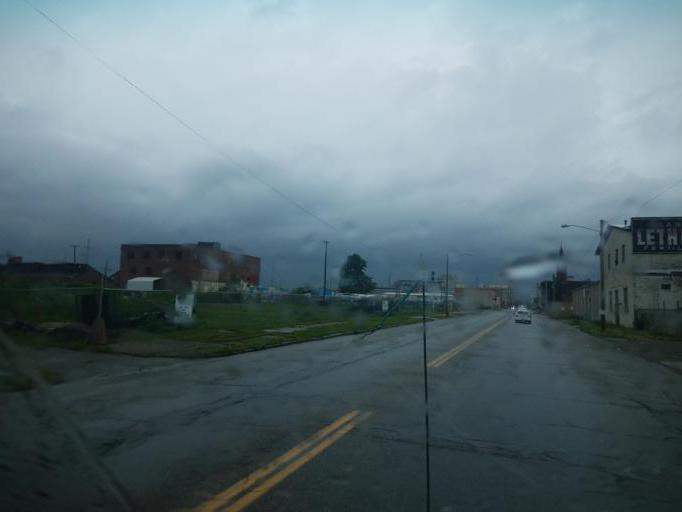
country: US
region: Ohio
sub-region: Stark County
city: Canton
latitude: 40.7963
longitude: -81.3638
